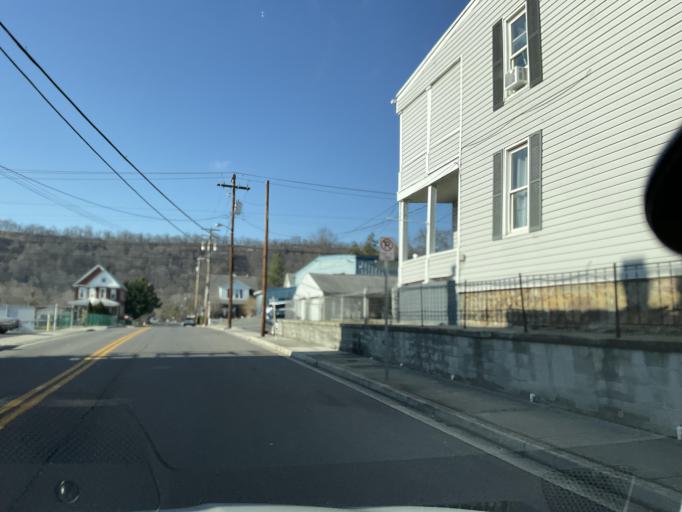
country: US
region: West Virginia
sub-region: Mineral County
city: Wiley Ford
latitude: 39.6284
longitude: -78.7676
